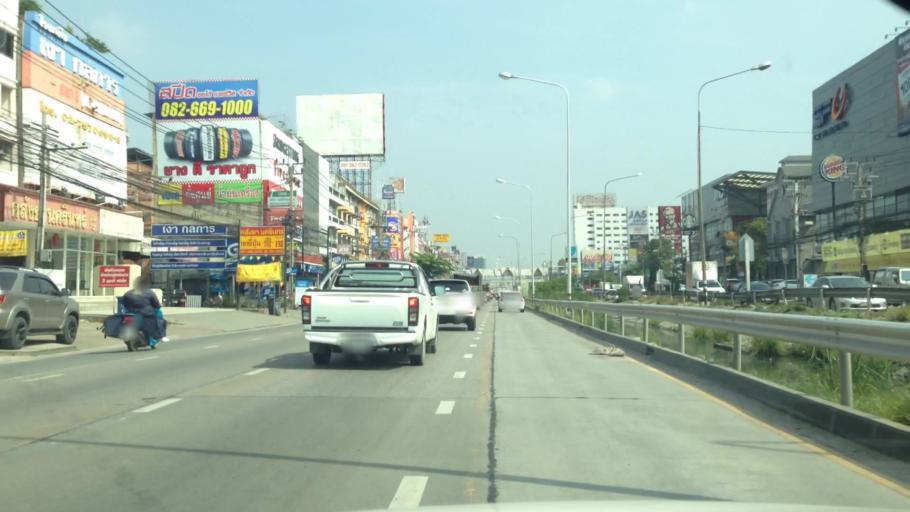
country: TH
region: Bangkok
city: Bang Na
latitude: 13.6345
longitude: 100.6308
